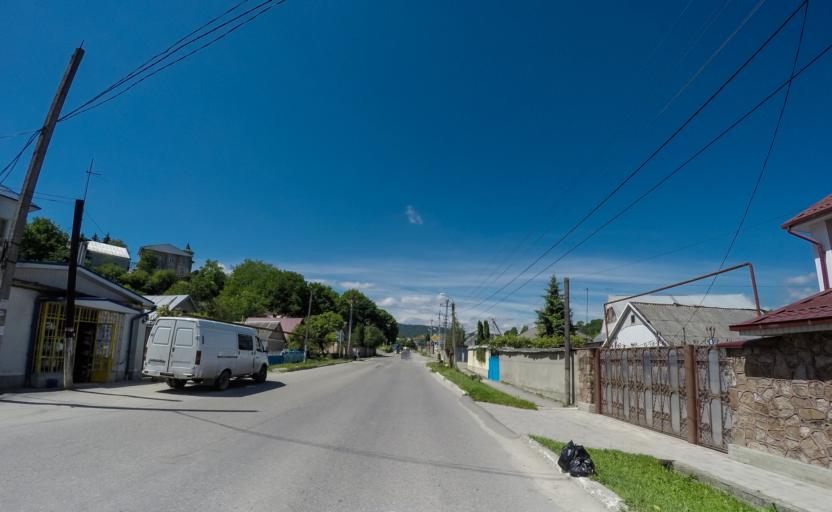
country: RU
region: Kabardino-Balkariya
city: Belaya Rechka
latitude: 43.4395
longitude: 43.5800
